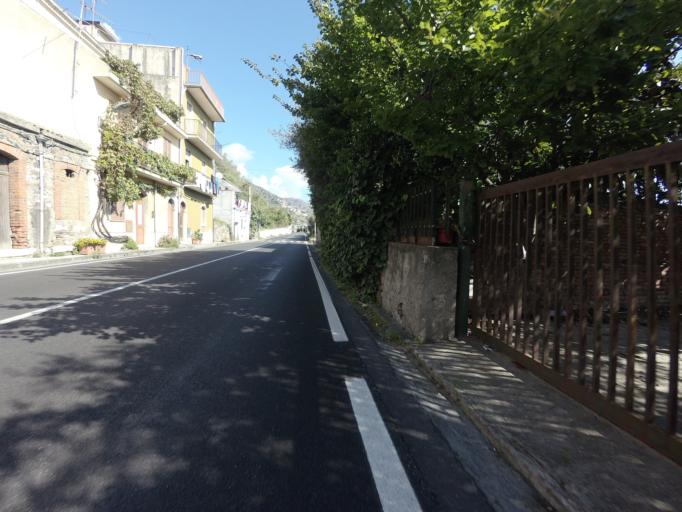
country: IT
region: Sicily
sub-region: Messina
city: Letojanni
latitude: 37.8728
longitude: 15.3002
